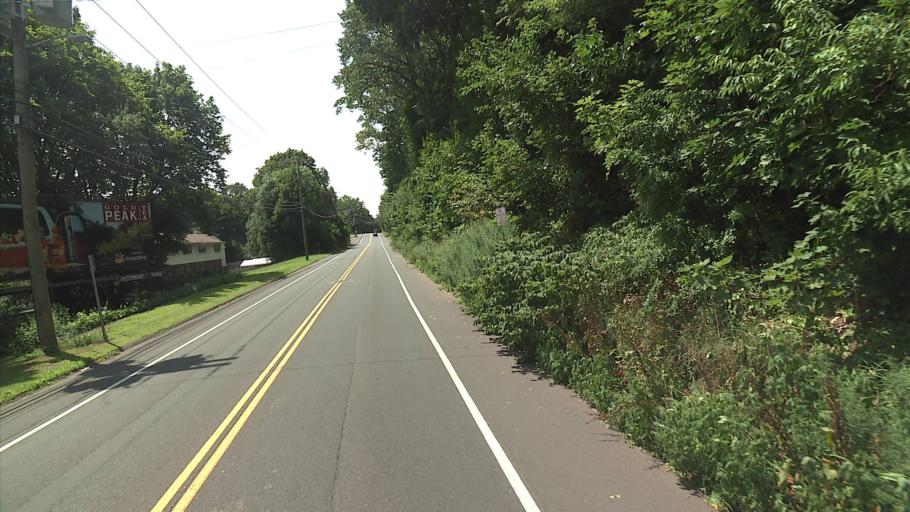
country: US
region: Connecticut
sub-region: New Haven County
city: Meriden
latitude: 41.5266
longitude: -72.8086
